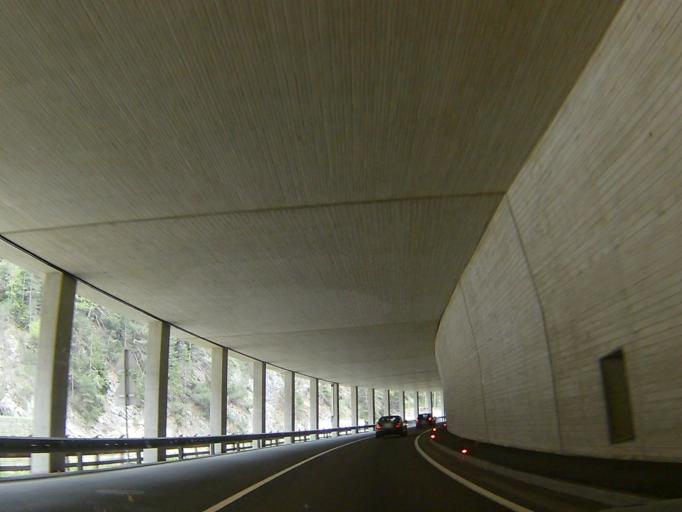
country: AT
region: Tyrol
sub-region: Politischer Bezirk Landeck
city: Nauders
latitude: 46.9135
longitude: 10.4934
